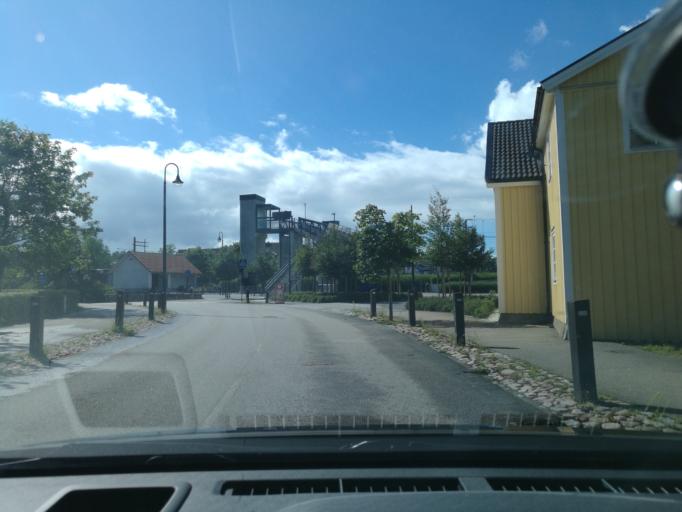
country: SE
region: Kronoberg
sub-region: Alvesta Kommun
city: Vislanda
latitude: 56.7863
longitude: 14.4556
